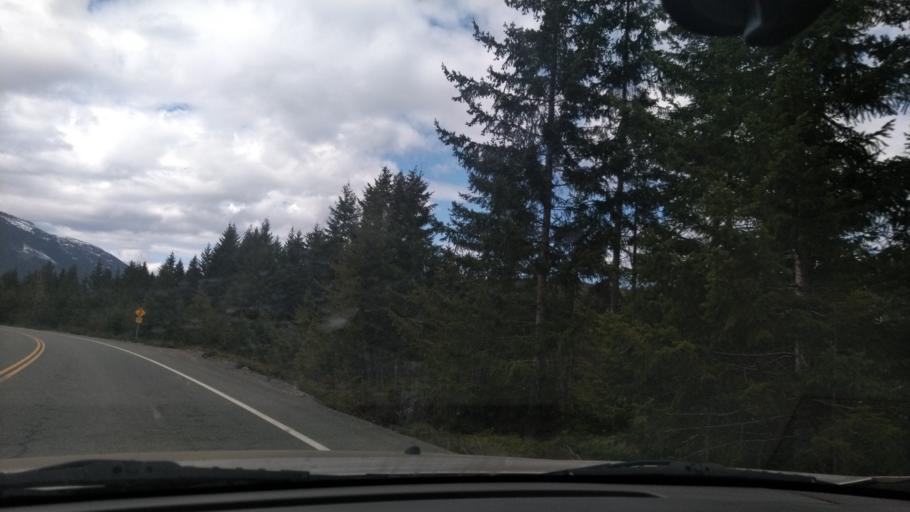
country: CA
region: British Columbia
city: Campbell River
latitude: 49.8672
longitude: -125.6469
